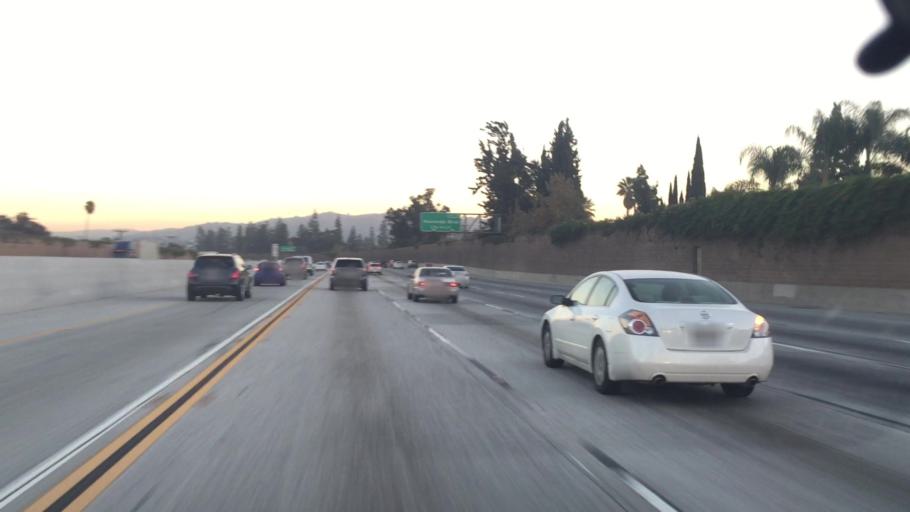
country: US
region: California
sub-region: Los Angeles County
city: Avocado Heights
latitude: 34.0153
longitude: -117.9845
